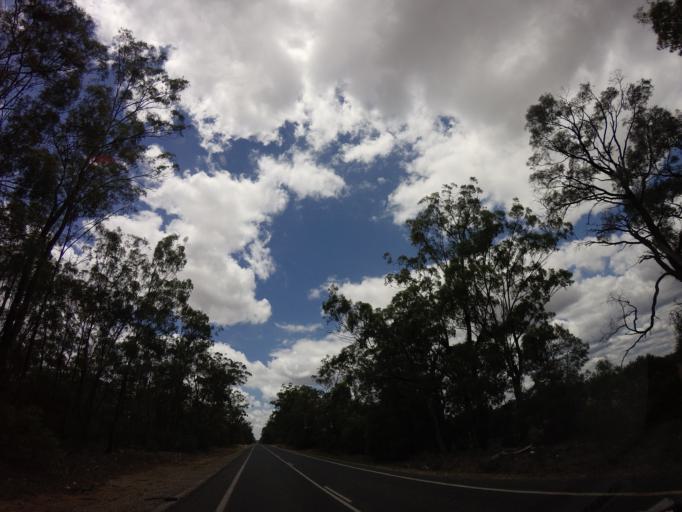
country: AU
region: Queensland
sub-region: Goondiwindi
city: Goondiwindi
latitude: -28.0209
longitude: 150.8532
